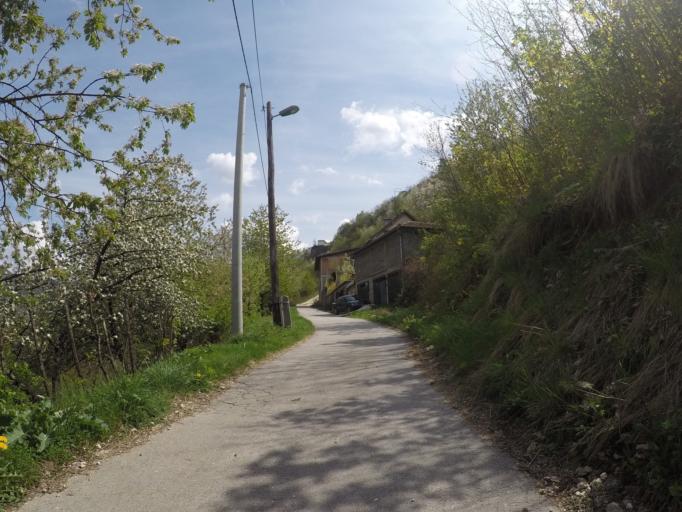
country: BA
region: Federation of Bosnia and Herzegovina
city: Kobilja Glava
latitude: 43.8569
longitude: 18.4432
